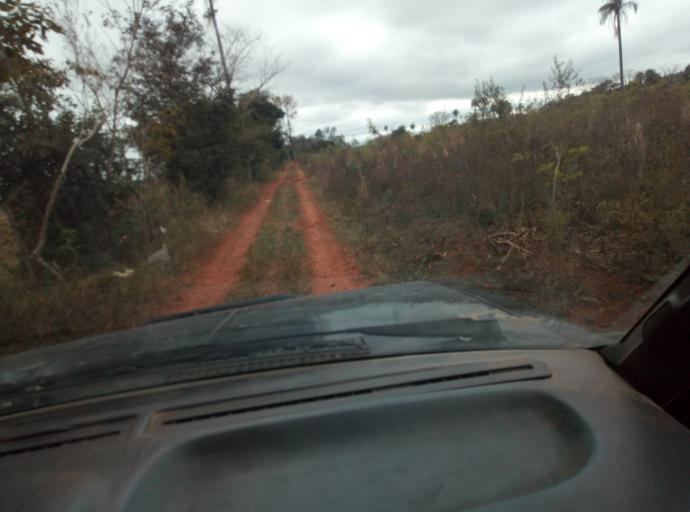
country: PY
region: Caaguazu
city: Doctor Cecilio Baez
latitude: -25.1454
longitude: -56.2917
